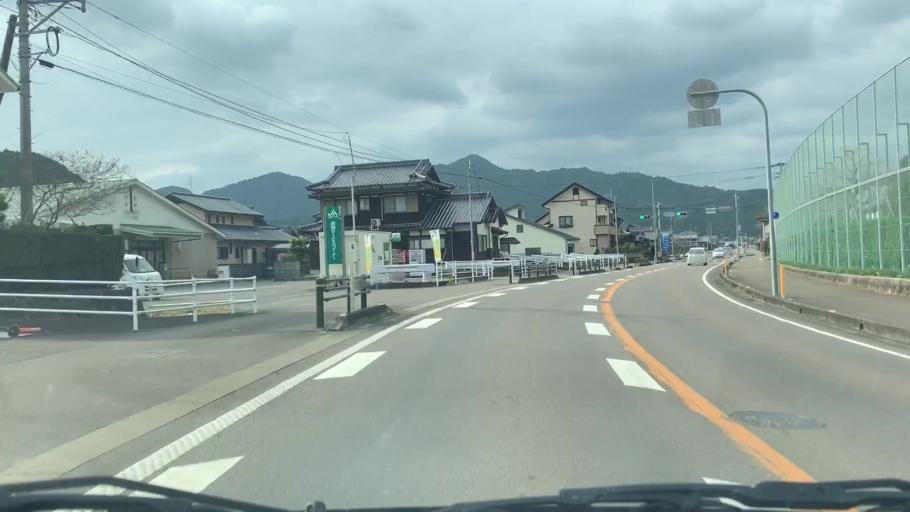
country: JP
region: Saga Prefecture
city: Ureshinomachi-shimojuku
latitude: 33.1262
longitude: 130.0452
